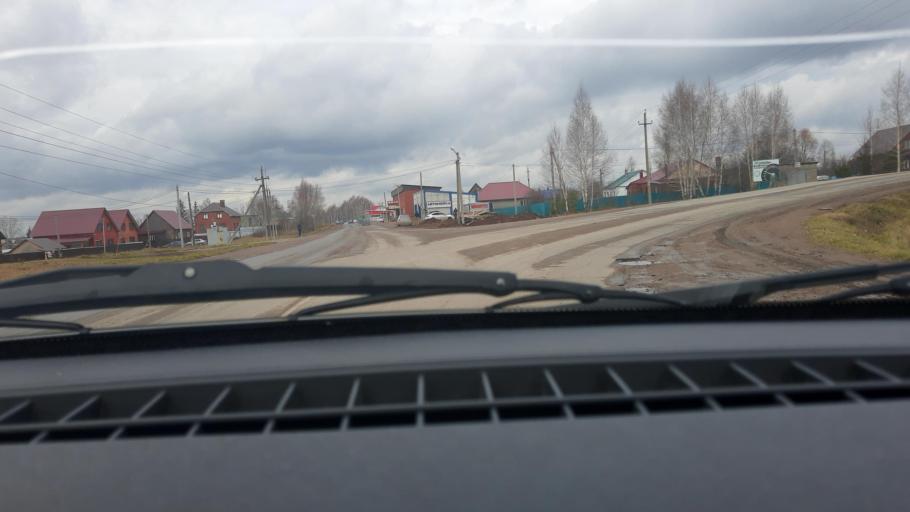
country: RU
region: Bashkortostan
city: Iglino
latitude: 54.8114
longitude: 56.4092
